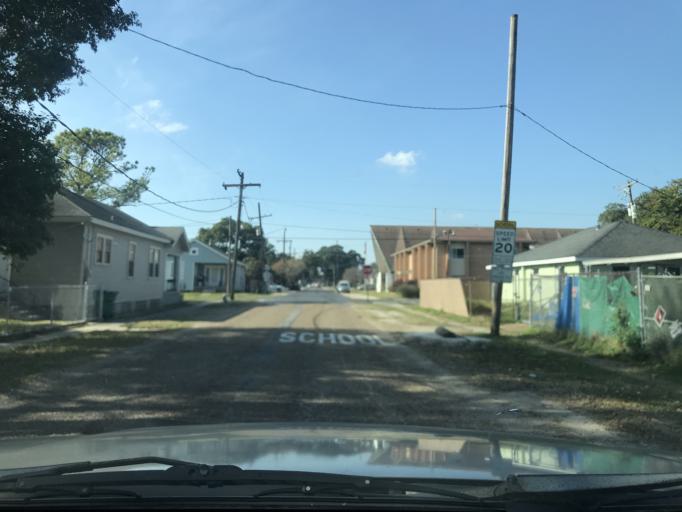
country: US
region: Louisiana
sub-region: Jefferson Parish
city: Marrero
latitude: 29.8993
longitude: -90.0940
